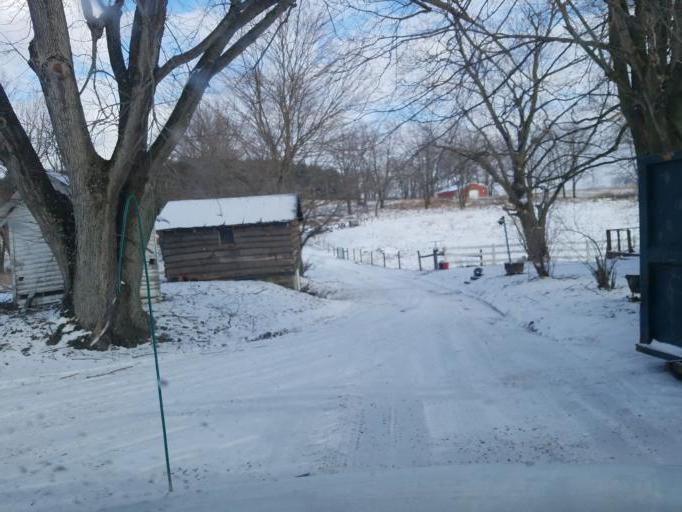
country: US
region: Ohio
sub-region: Holmes County
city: Millersburg
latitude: 40.4543
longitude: -81.9380
